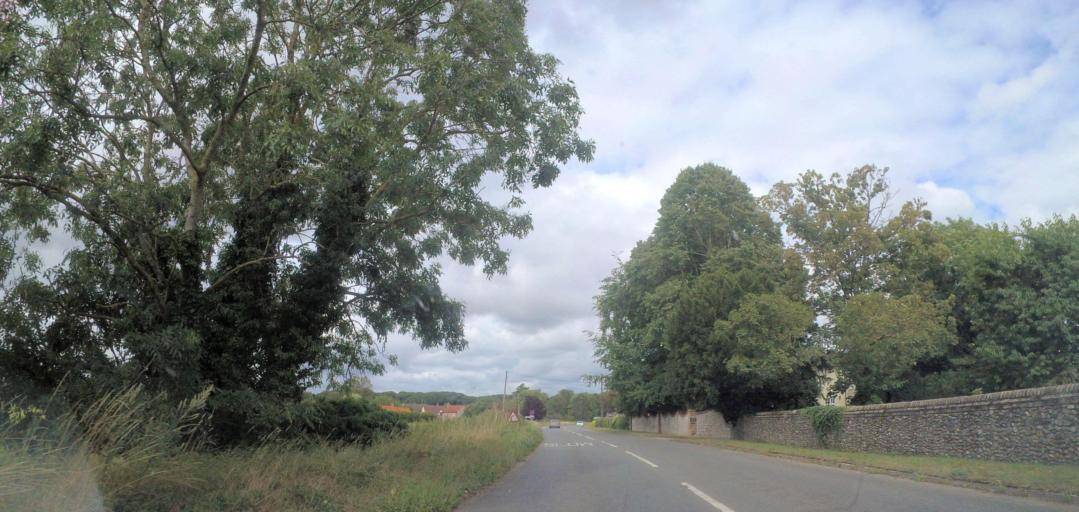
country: GB
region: England
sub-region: Suffolk
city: Lakenheath
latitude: 52.3324
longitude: 0.5210
